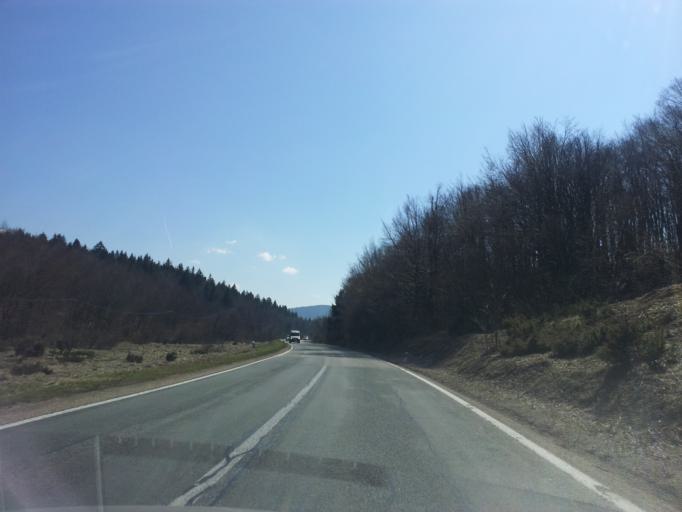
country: HR
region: Licko-Senjska
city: Jezerce
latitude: 44.8261
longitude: 15.6741
